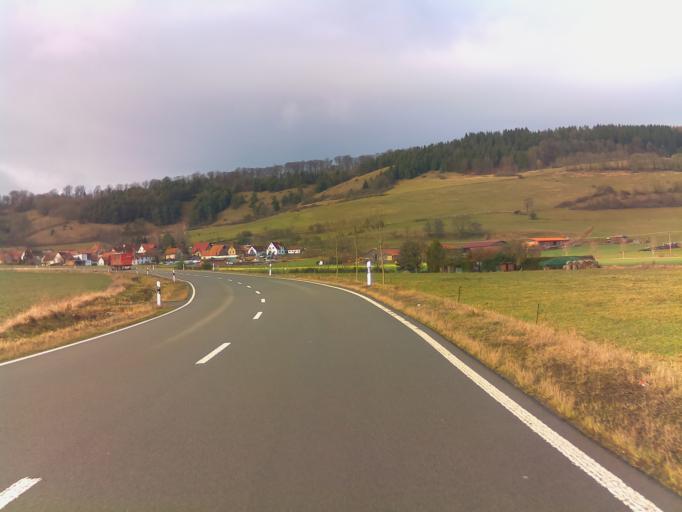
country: DE
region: Thuringia
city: Dermbach
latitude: 50.7225
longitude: 10.1050
